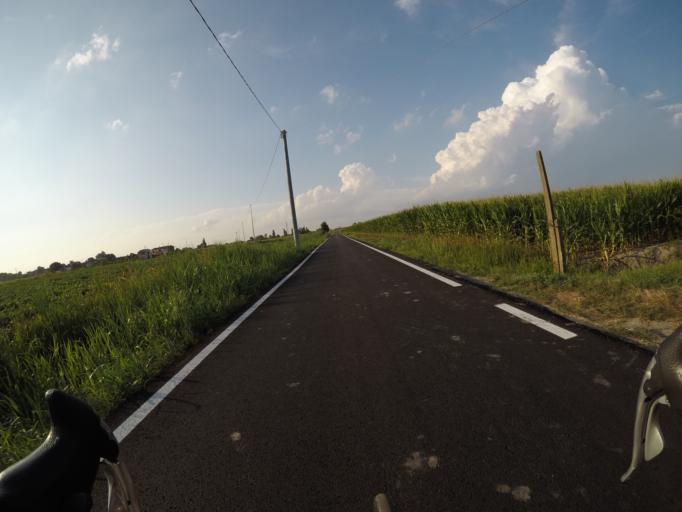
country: IT
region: Veneto
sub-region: Provincia di Rovigo
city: San Bellino
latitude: 45.0421
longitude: 11.5902
